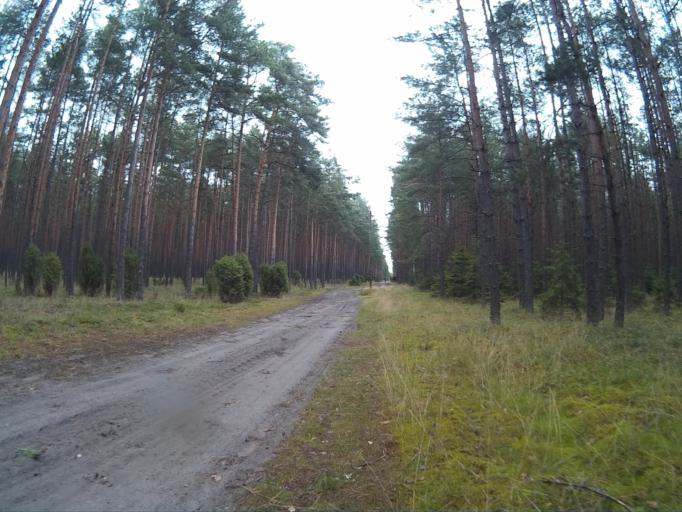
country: PL
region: Kujawsko-Pomorskie
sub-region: Powiat swiecki
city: Osie
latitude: 53.6129
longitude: 18.3968
